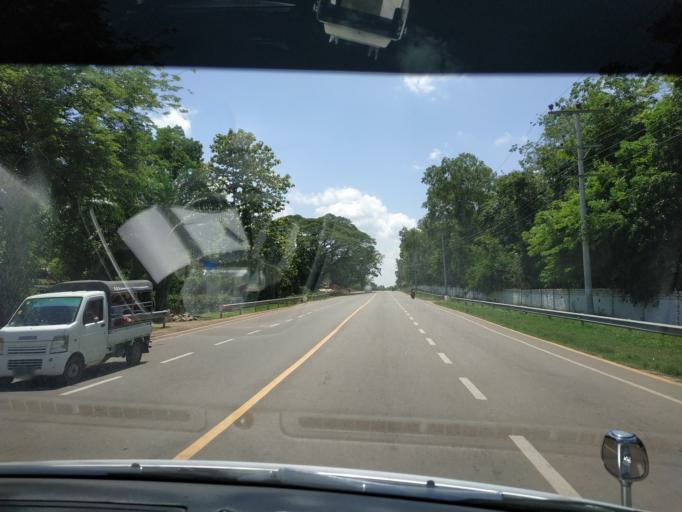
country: MM
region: Mon
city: Kyaikto
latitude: 17.3123
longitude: 97.0237
